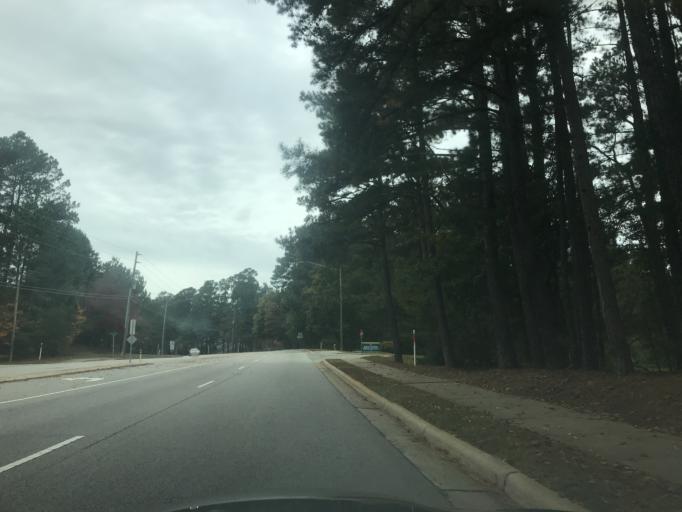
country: US
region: North Carolina
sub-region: Wake County
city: West Raleigh
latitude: 35.8575
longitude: -78.6655
